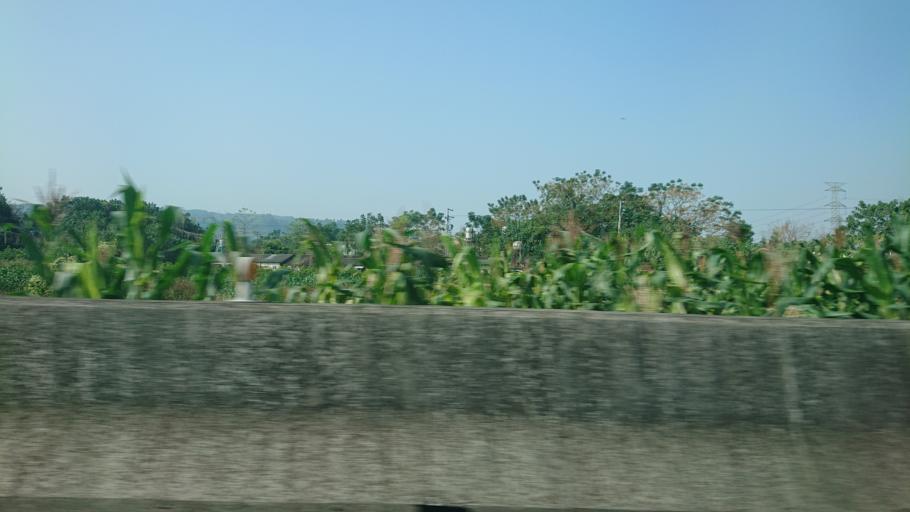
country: TW
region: Taiwan
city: Lugu
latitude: 23.7682
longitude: 120.6595
